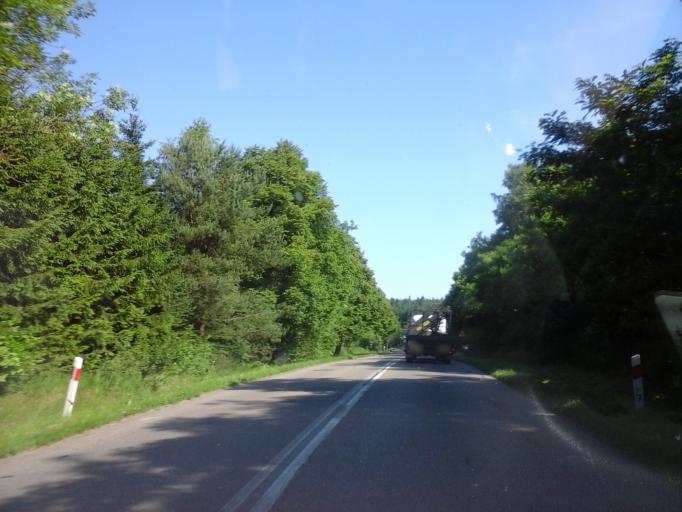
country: PL
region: West Pomeranian Voivodeship
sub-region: Powiat swidwinski
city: Polczyn-Zdroj
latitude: 53.7855
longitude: 16.0729
